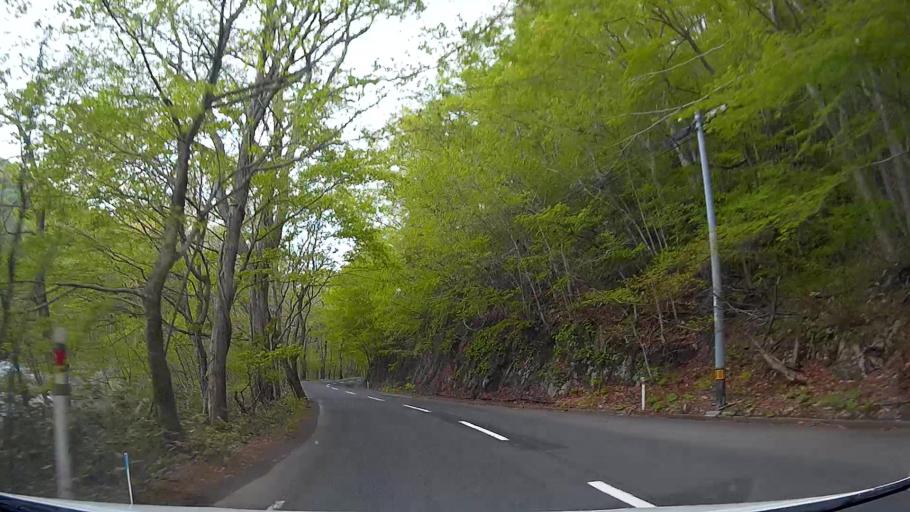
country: JP
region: Aomori
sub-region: Aomori Shi
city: Furudate
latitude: 40.5708
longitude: 140.9790
